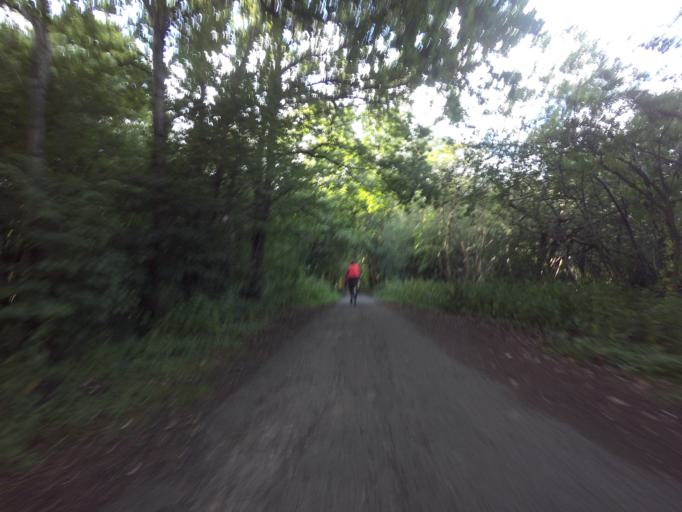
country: GB
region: England
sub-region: East Sussex
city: Horam
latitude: 50.9185
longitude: 0.2561
